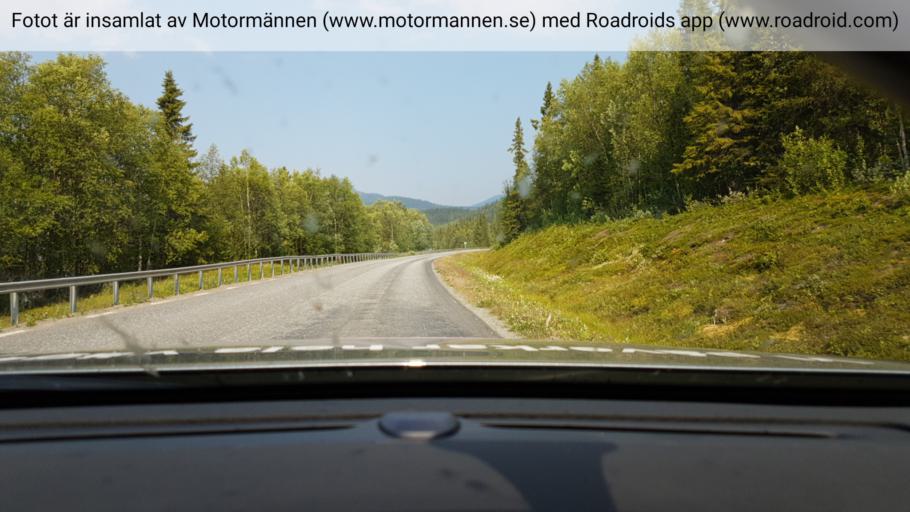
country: SE
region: Vaesterbotten
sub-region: Vilhelmina Kommun
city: Sjoberg
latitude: 65.4931
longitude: 15.7869
